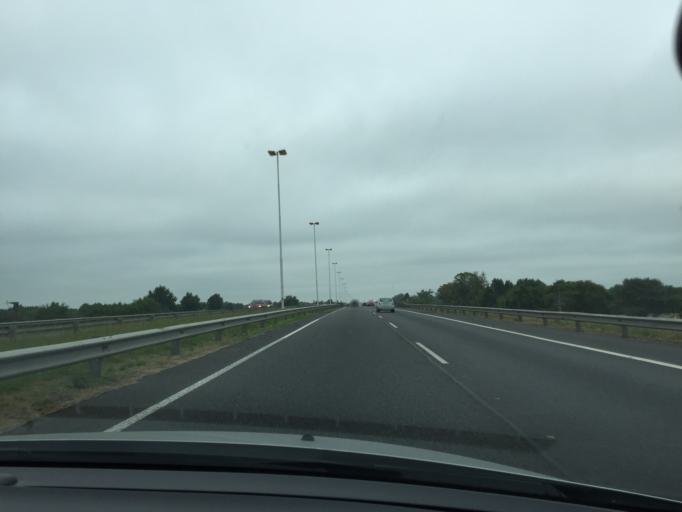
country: AR
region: Buenos Aires
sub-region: Partido de Ezeiza
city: Ezeiza
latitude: -34.8491
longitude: -58.5424
